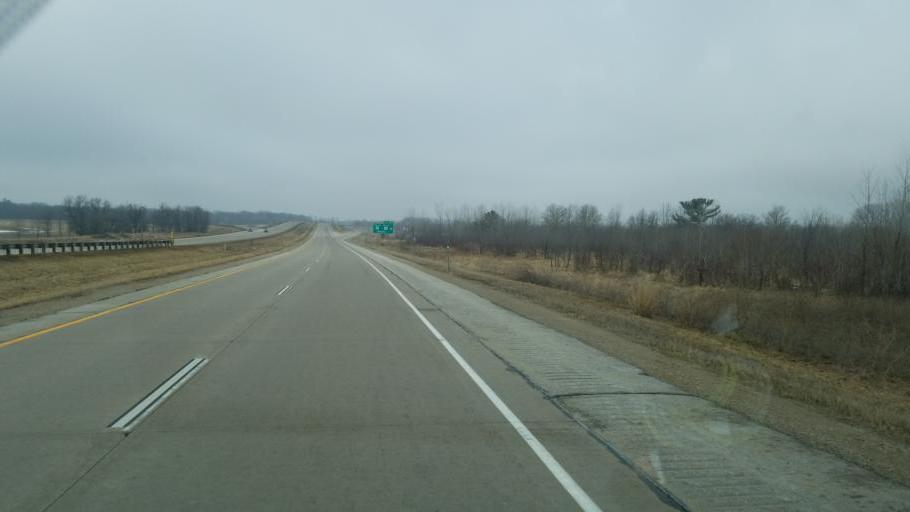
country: US
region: Wisconsin
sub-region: Waupaca County
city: Weyauwega
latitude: 44.2630
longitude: -88.9019
